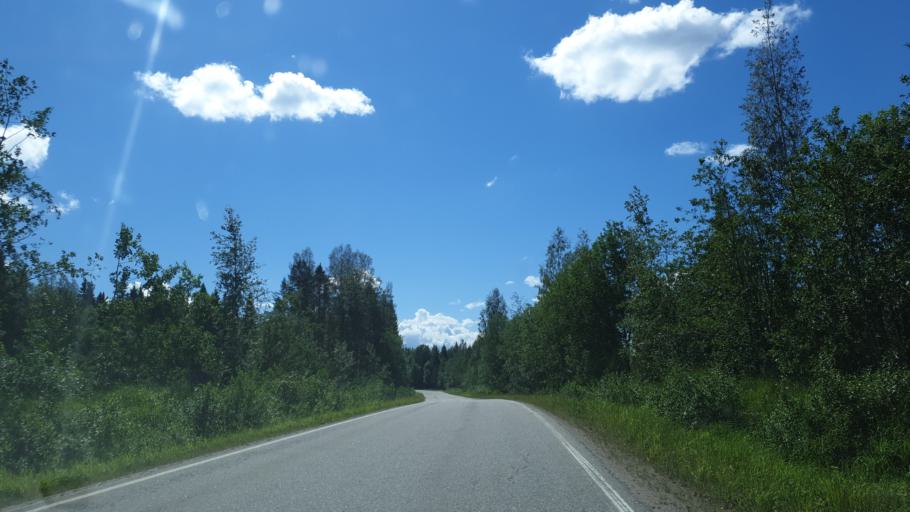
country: FI
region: Northern Savo
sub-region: Koillis-Savo
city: Kaavi
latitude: 63.0135
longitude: 28.5177
